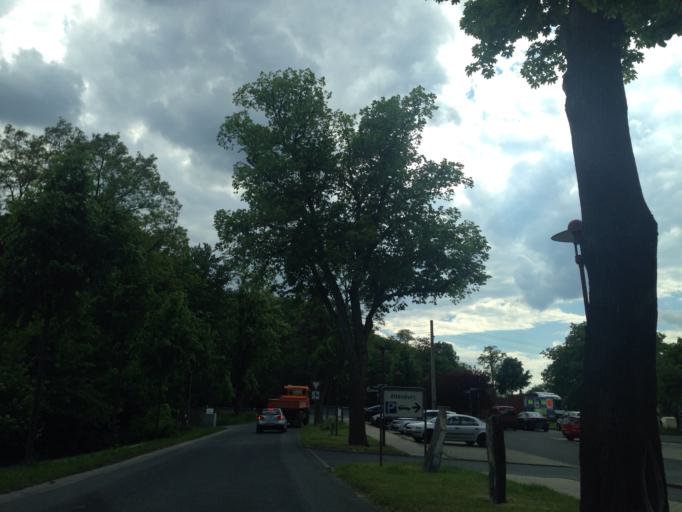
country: DE
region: Thuringia
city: Possneck
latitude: 50.6900
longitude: 11.6005
